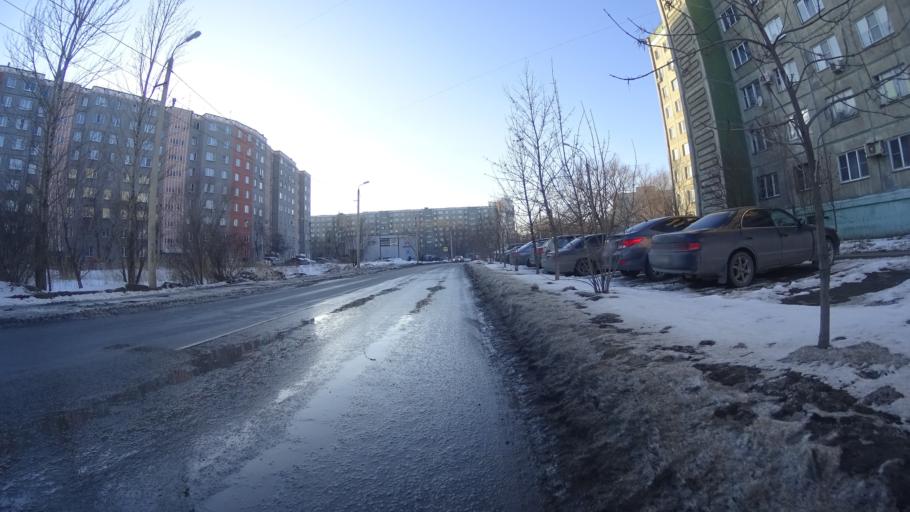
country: RU
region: Chelyabinsk
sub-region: Gorod Chelyabinsk
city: Chelyabinsk
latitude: 55.1364
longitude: 61.4509
